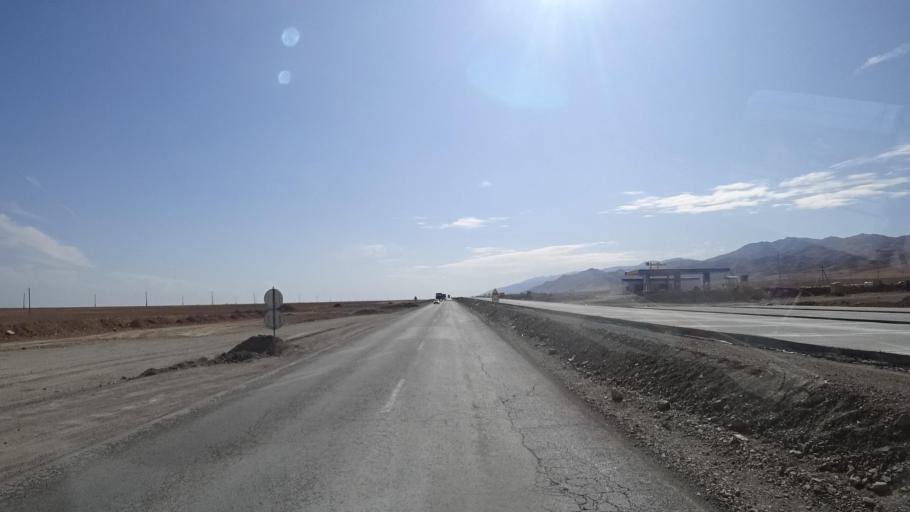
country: KG
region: Chuy
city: Ivanovka
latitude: 43.4001
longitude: 75.1152
